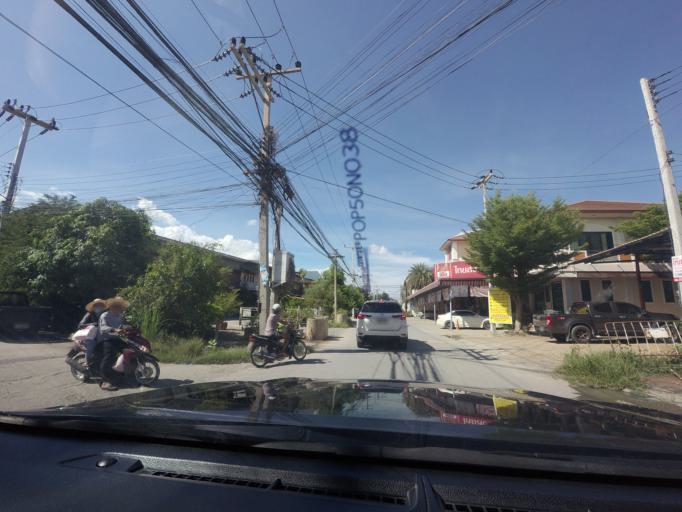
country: TH
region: Suphan Buri
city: Song Phi Nong
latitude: 14.1794
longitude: 99.9389
